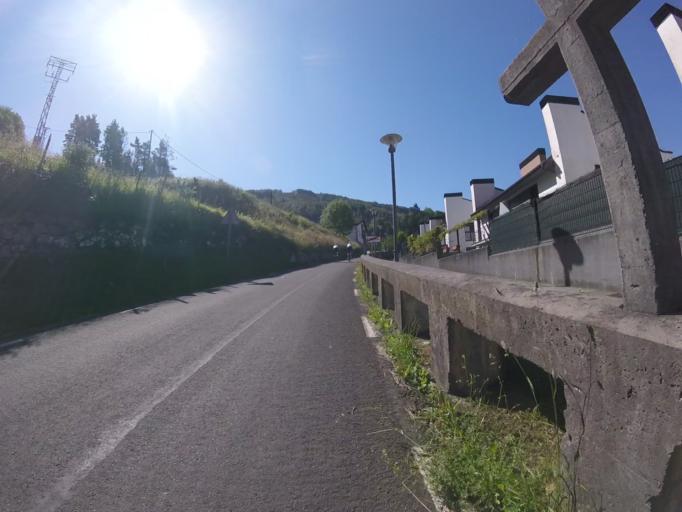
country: ES
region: Basque Country
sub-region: Provincia de Guipuzcoa
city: Beizama
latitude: 43.1337
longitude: -2.1989
